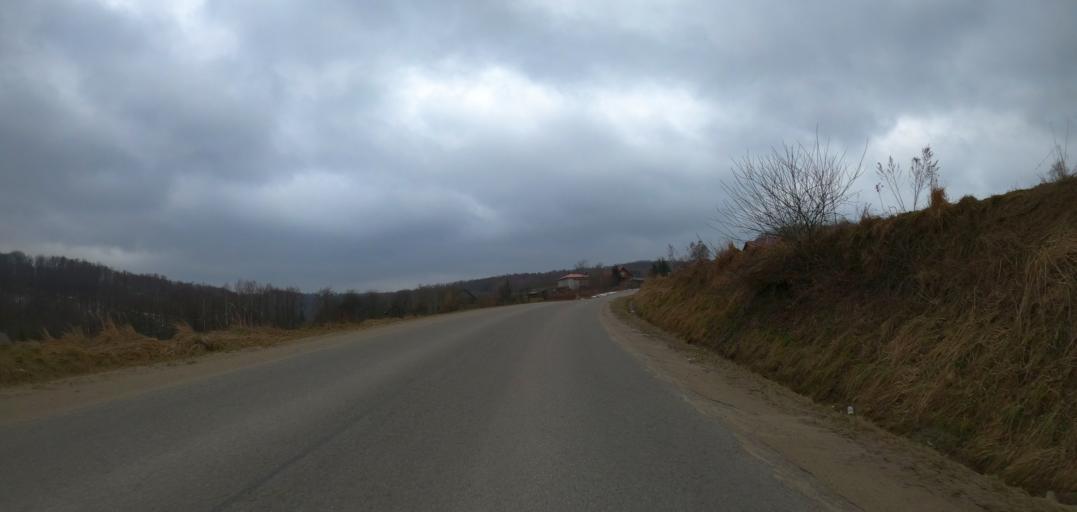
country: PL
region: Subcarpathian Voivodeship
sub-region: Powiat debicki
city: Debica
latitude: 49.9853
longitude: 21.4137
